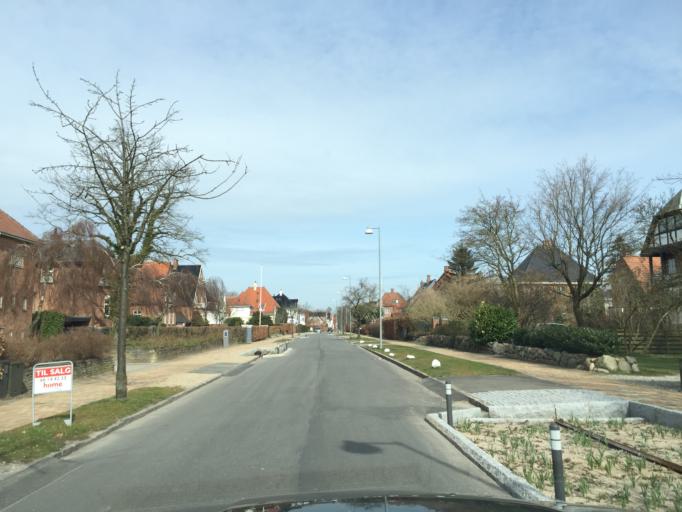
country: DK
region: South Denmark
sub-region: Odense Kommune
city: Odense
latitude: 55.3839
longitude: 10.3779
